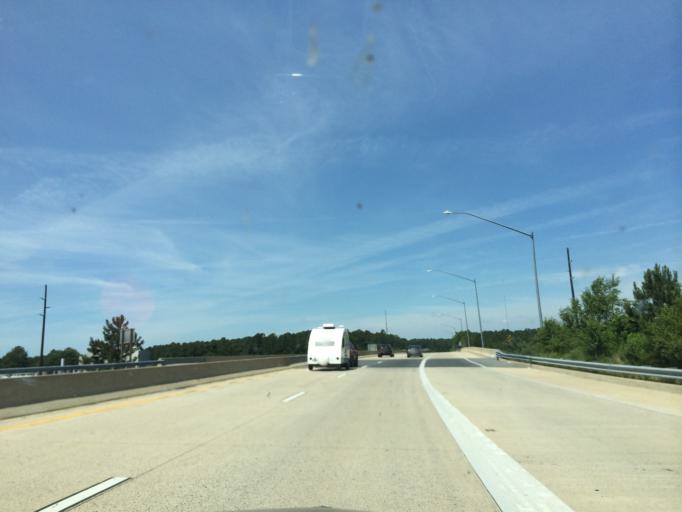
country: US
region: Maryland
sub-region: Wicomico County
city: Salisbury
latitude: 38.4025
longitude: -75.5836
